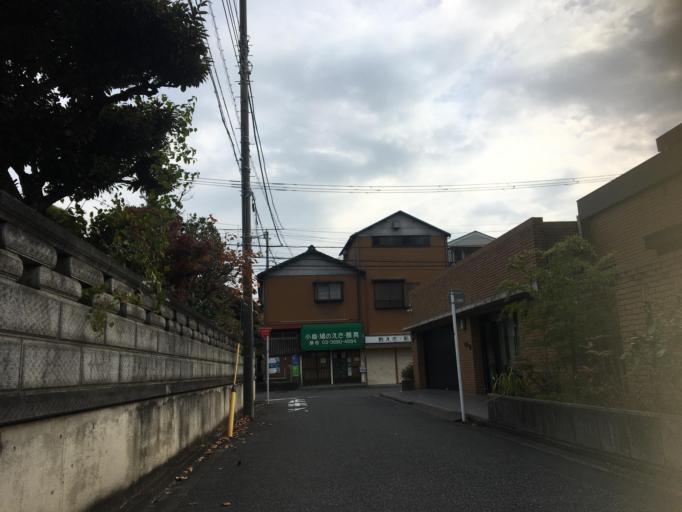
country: JP
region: Tokyo
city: Urayasu
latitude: 35.6581
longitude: 139.8842
